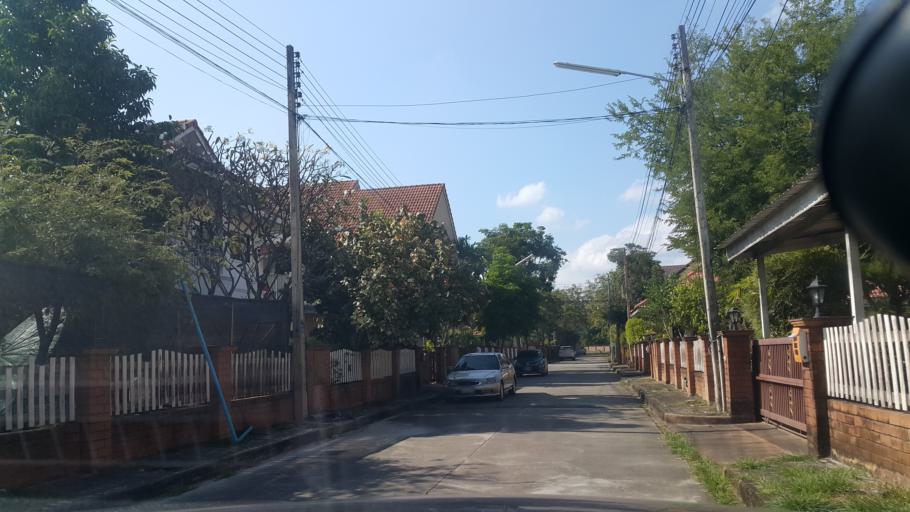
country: TH
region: Chiang Mai
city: Hang Dong
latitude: 18.7299
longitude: 98.9463
